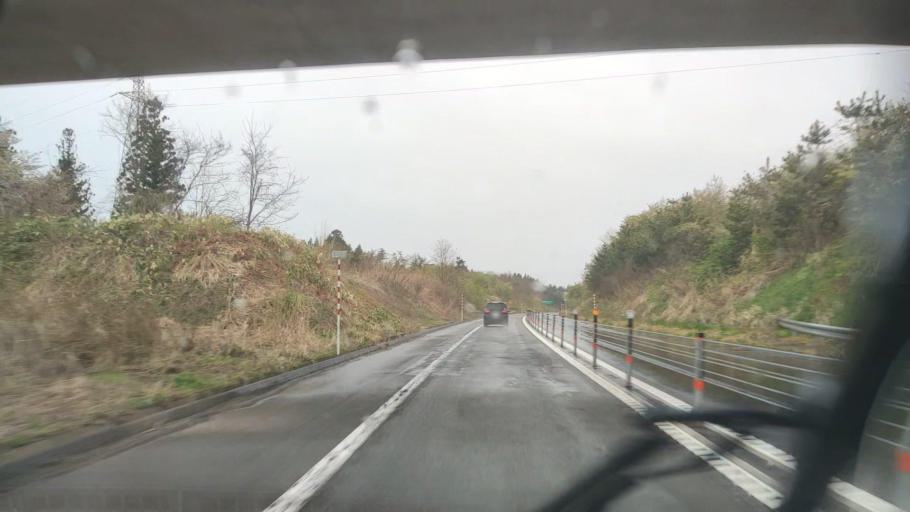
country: JP
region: Akita
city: Noshiromachi
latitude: 40.1651
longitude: 140.0474
